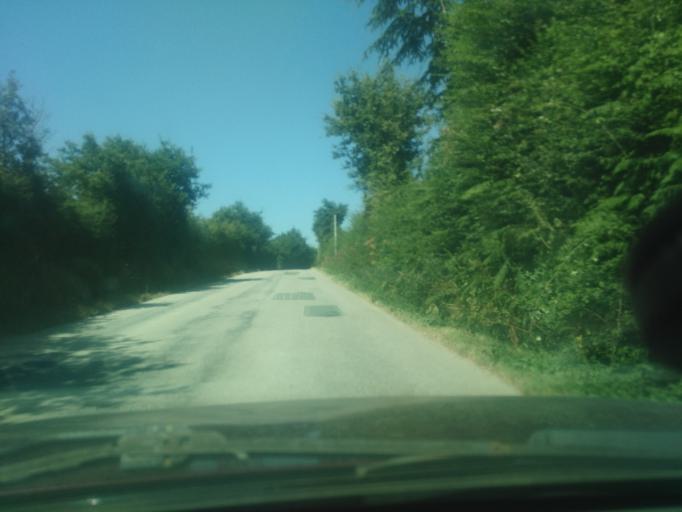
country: FR
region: Pays de la Loire
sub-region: Departement de la Vendee
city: Dompierre-sur-Yon
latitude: 46.7190
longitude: -1.3952
